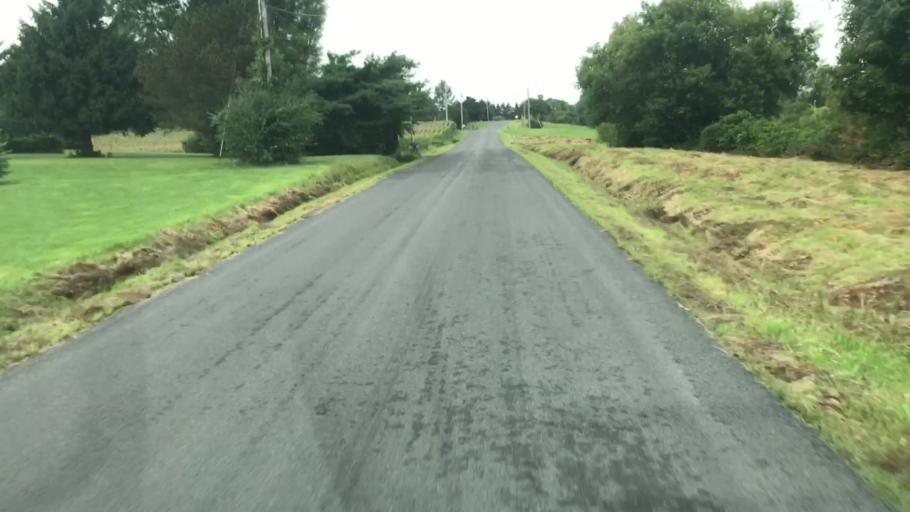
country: US
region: New York
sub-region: Cayuga County
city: Auburn
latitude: 42.9752
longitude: -76.5093
